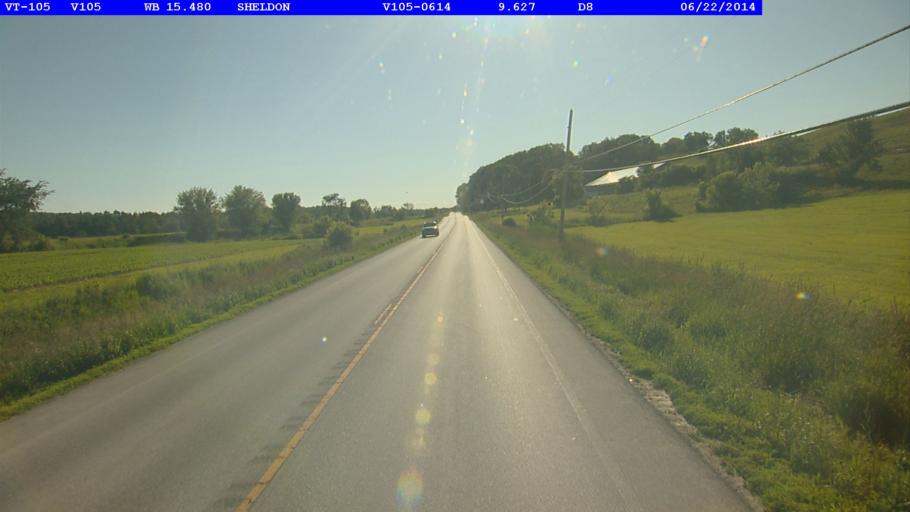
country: US
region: Vermont
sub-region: Franklin County
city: Enosburg Falls
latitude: 44.9088
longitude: -72.8476
